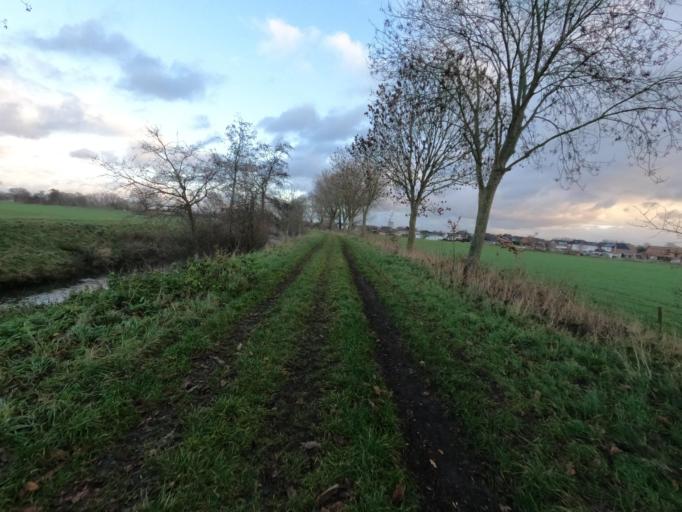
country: DE
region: North Rhine-Westphalia
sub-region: Regierungsbezirk Koln
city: Heinsberg
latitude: 51.0887
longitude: 6.1132
